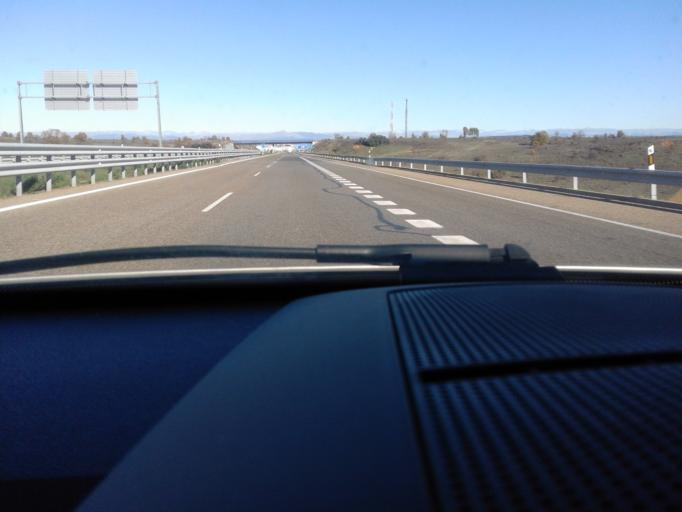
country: ES
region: Castille and Leon
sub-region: Provincia de Leon
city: Onzonilla
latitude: 42.5111
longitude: -5.5963
